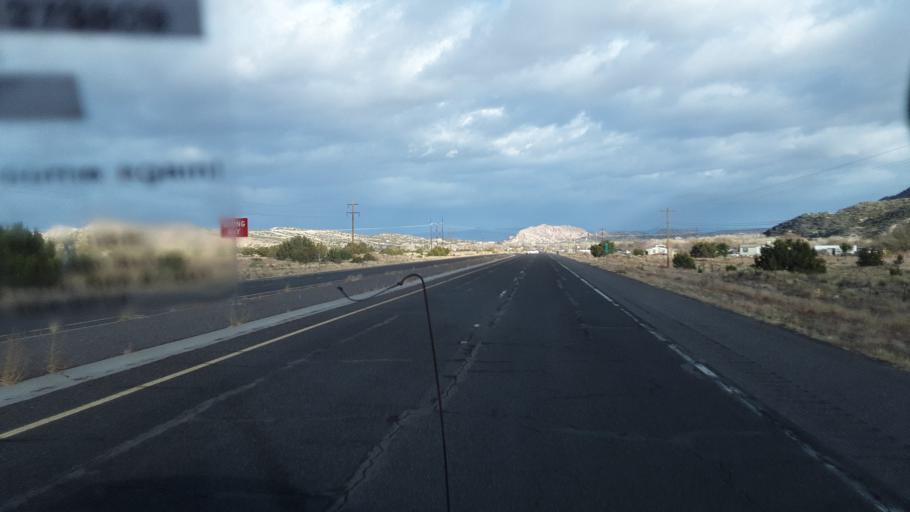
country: US
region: New Mexico
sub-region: Rio Arriba County
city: Ohkay Owingeh
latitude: 36.0762
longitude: -106.1269
